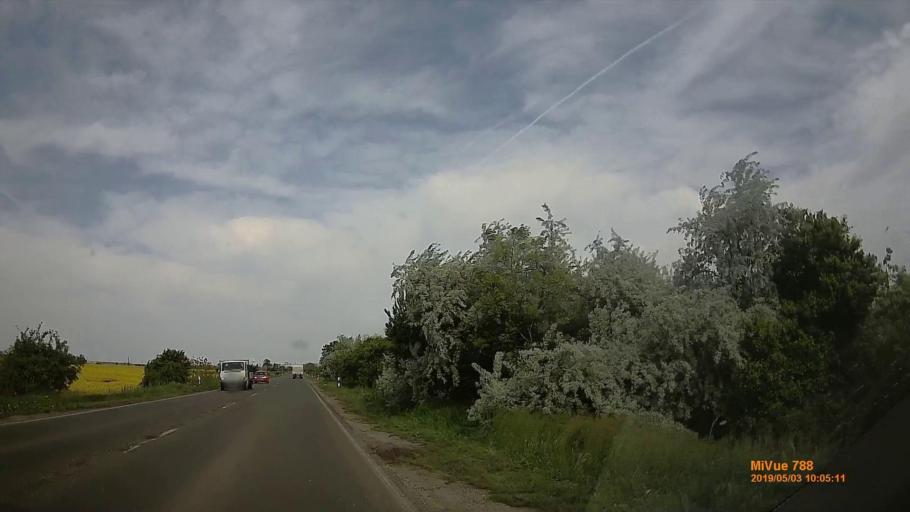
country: HU
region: Jasz-Nagykun-Szolnok
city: Torokszentmiklos
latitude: 47.1760
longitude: 20.3734
